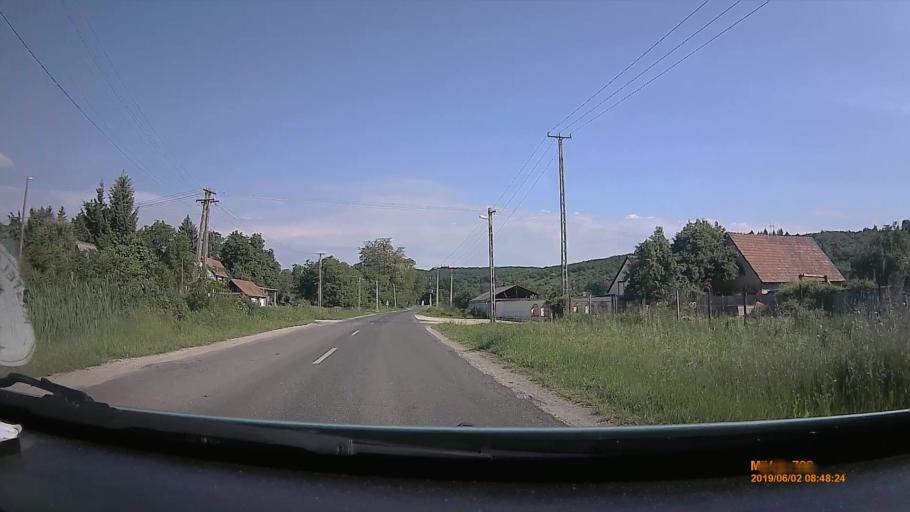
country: HU
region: Borsod-Abauj-Zemplen
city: Sajobabony
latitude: 48.1357
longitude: 20.7048
